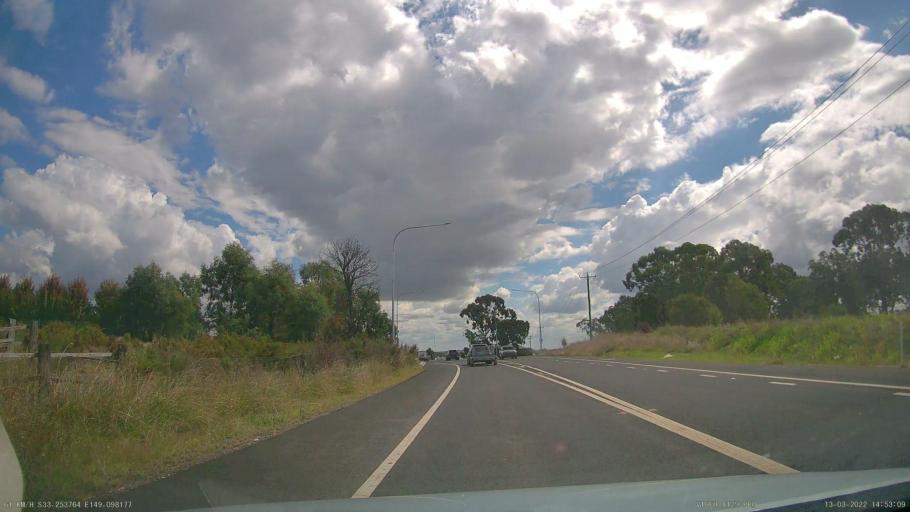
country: AU
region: New South Wales
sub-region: Orange Municipality
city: Orange
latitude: -33.2536
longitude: 149.0978
